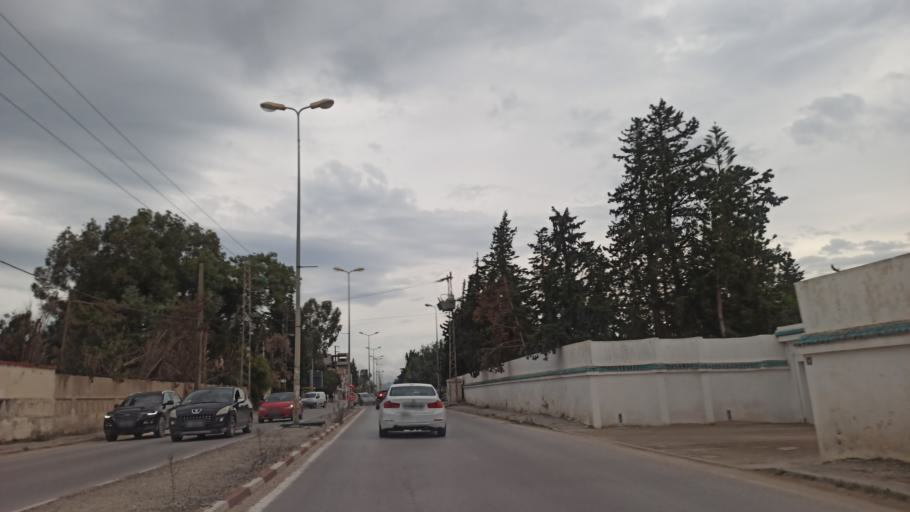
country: TN
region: Ariana
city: Ariana
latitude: 36.8717
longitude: 10.2478
